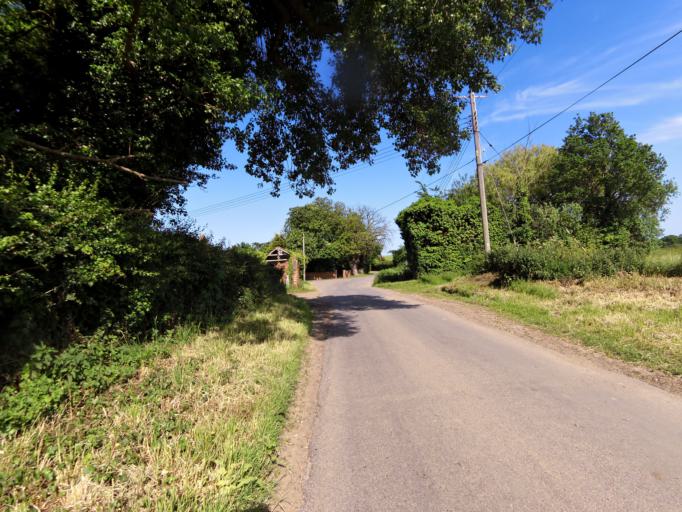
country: GB
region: England
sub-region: Suffolk
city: Felixstowe
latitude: 51.9816
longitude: 1.3540
